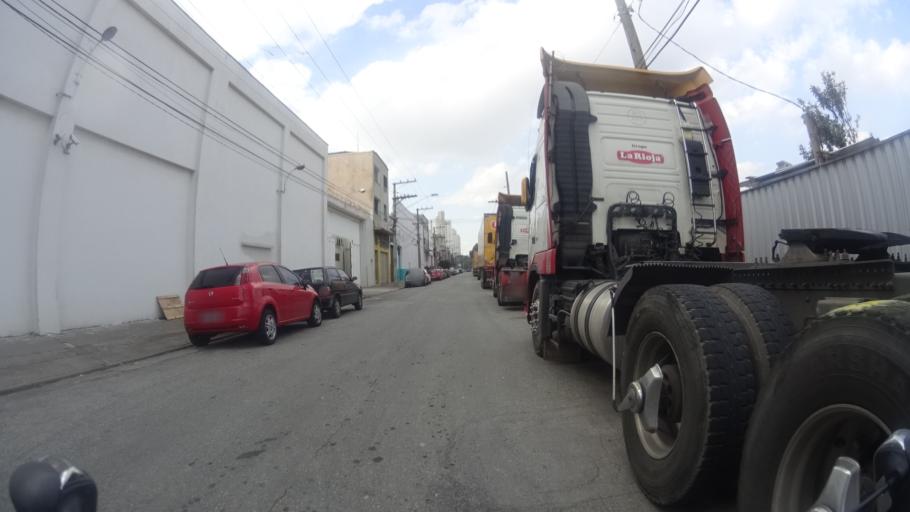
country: BR
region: Sao Paulo
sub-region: Sao Paulo
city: Sao Paulo
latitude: -23.5507
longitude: -46.6157
